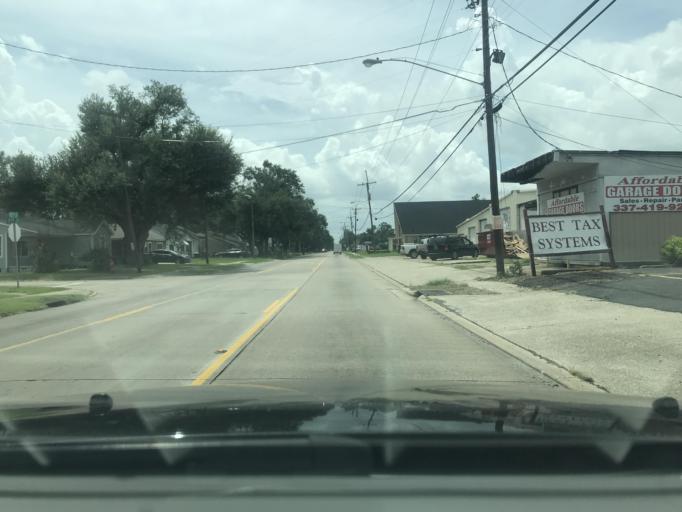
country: US
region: Louisiana
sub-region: Calcasieu Parish
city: Lake Charles
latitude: 30.2131
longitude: -93.1849
